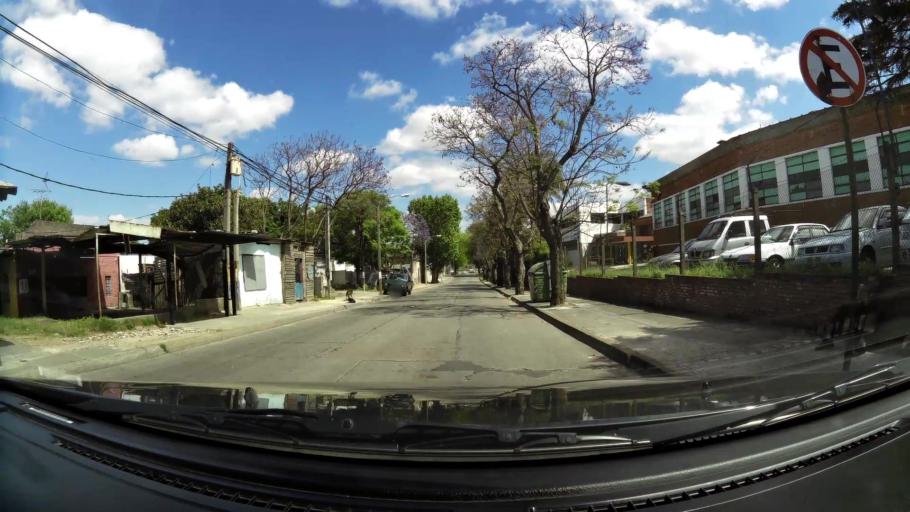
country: UY
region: Montevideo
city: Montevideo
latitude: -34.8604
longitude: -56.1420
